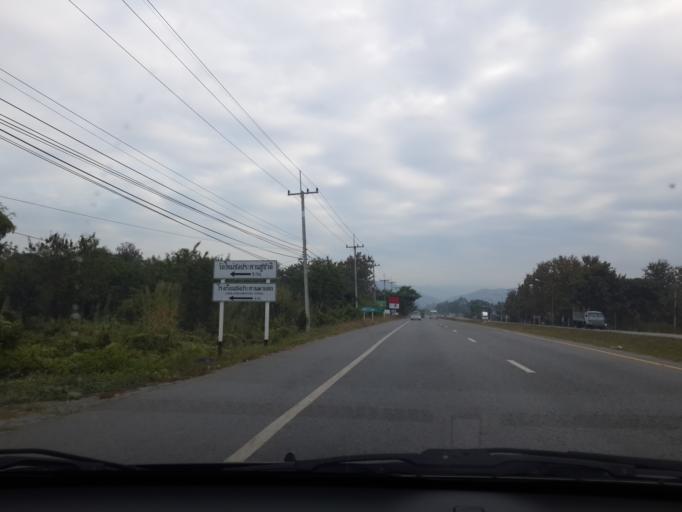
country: TH
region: Chiang Mai
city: San Sai
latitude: 18.8787
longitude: 99.1430
